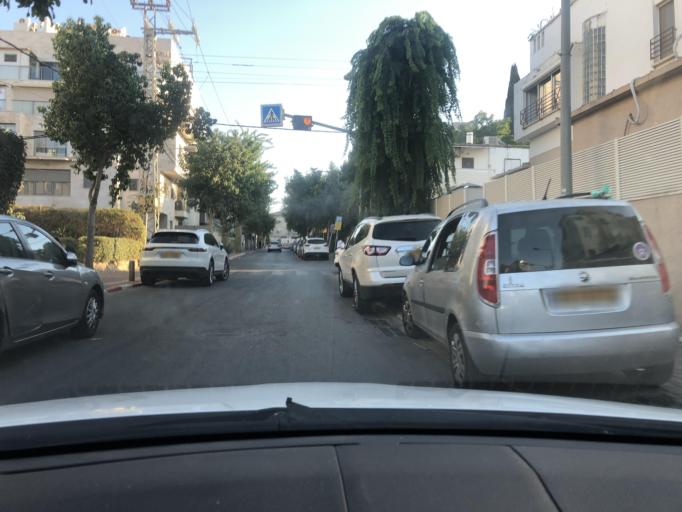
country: IL
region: Tel Aviv
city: Bene Beraq
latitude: 32.0773
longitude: 34.8289
